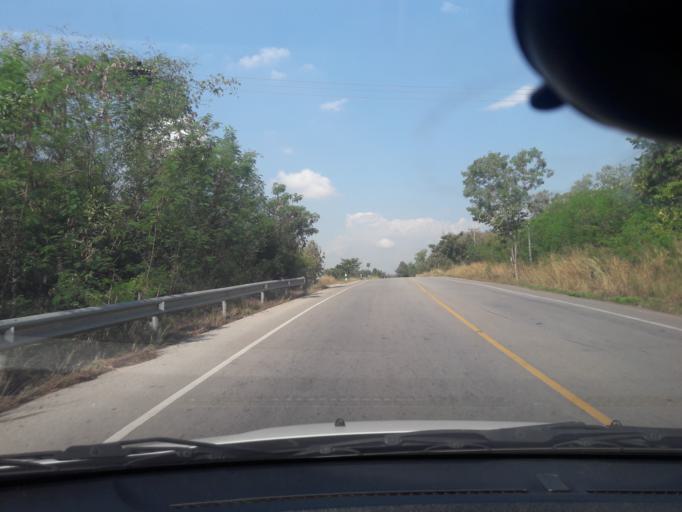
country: TH
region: Lampang
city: Mae Tha
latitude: 18.1939
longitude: 99.5171
